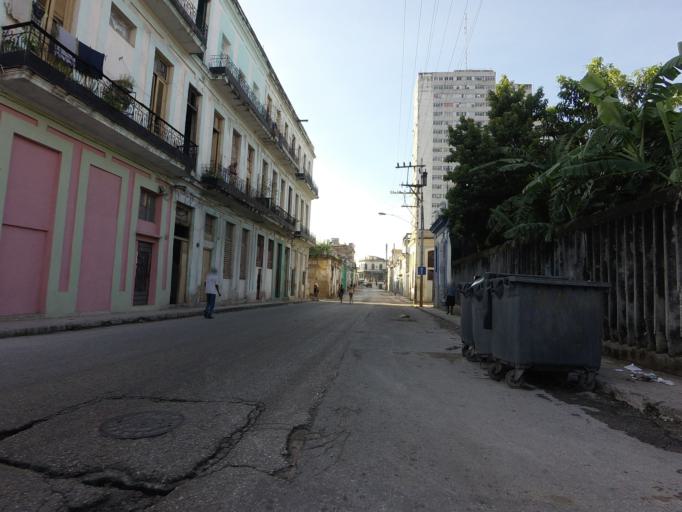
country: CU
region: La Habana
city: Cerro
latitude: 23.1189
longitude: -82.3716
